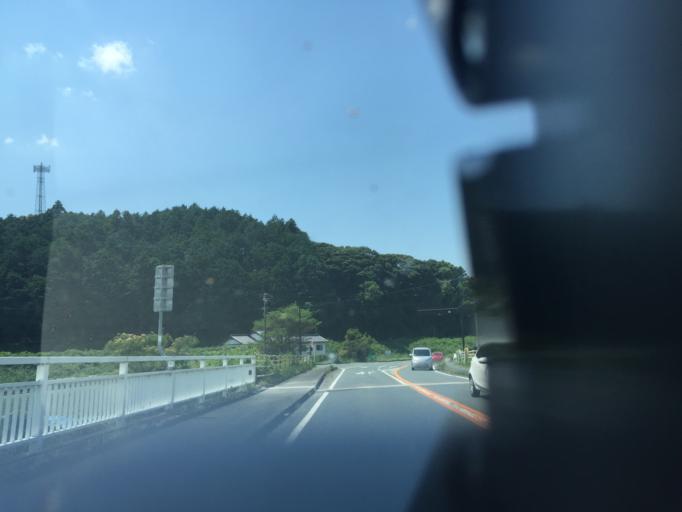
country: JP
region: Shizuoka
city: Mori
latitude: 34.8178
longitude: 137.9544
